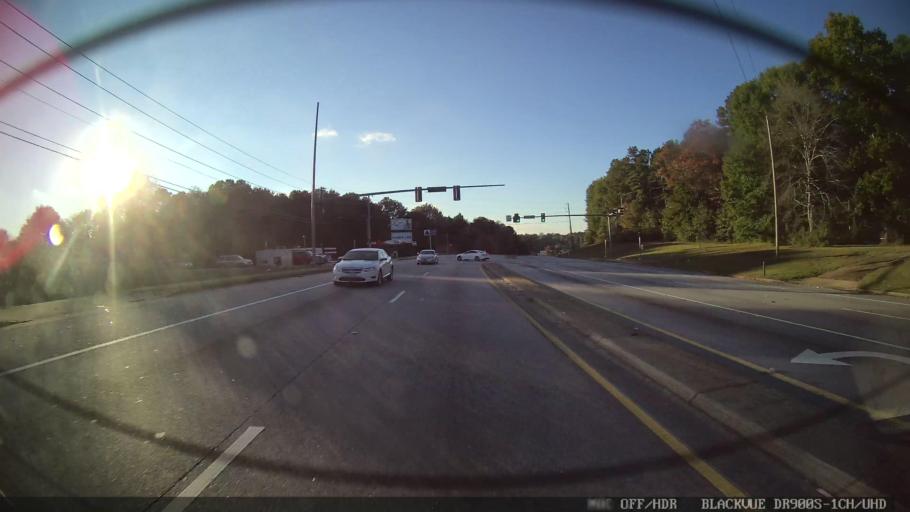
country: US
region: Georgia
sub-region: Clayton County
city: Morrow
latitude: 33.5778
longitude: -84.2865
